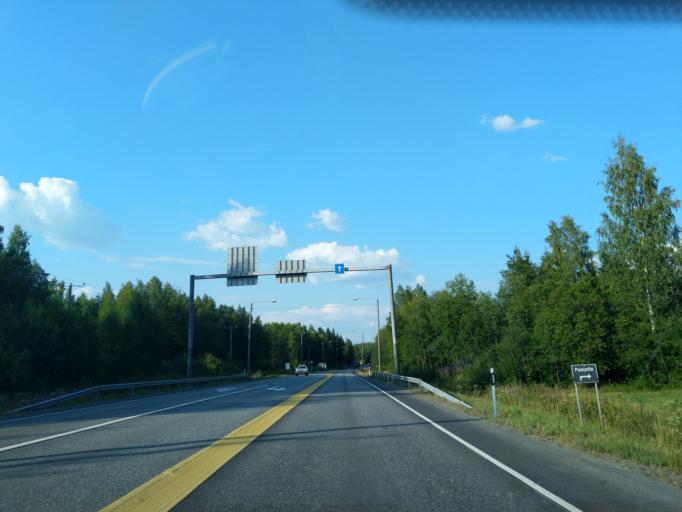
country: FI
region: Satakunta
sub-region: Pori
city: Pomarkku
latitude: 61.7002
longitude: 22.0116
